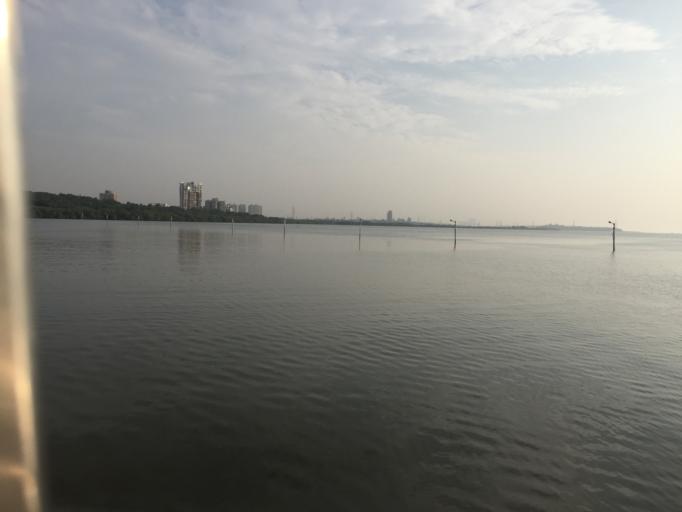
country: IN
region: Maharashtra
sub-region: Mumbai Suburban
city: Borivli
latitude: 19.2251
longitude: 72.8092
